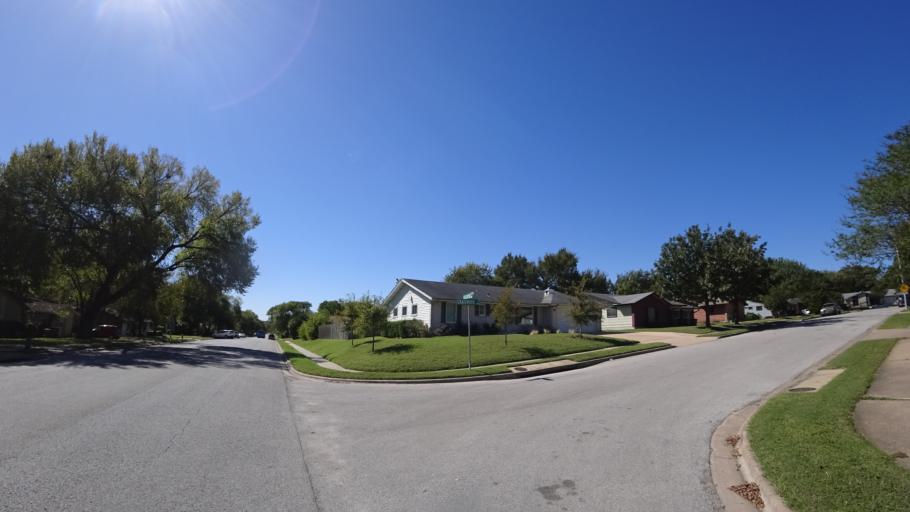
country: US
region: Texas
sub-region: Travis County
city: Austin
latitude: 30.2837
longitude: -97.6601
